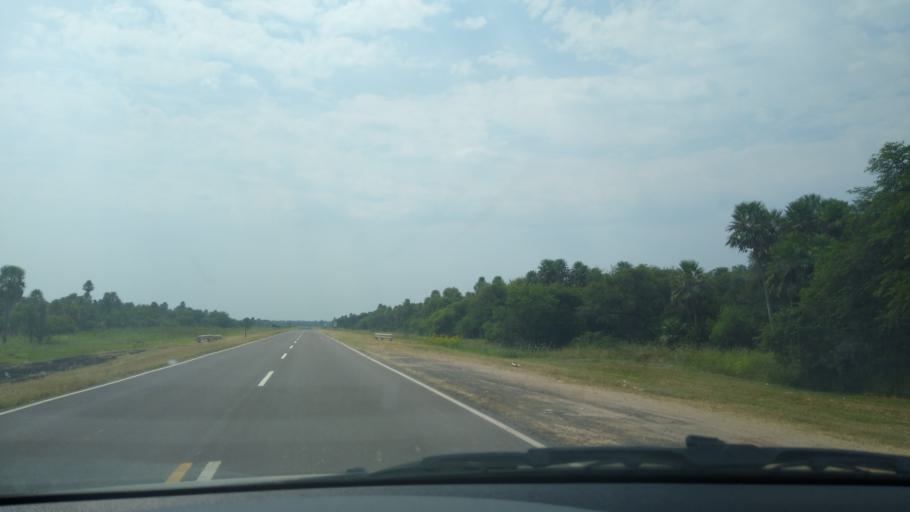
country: AR
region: Chaco
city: Margarita Belen
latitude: -27.0814
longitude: -58.9601
